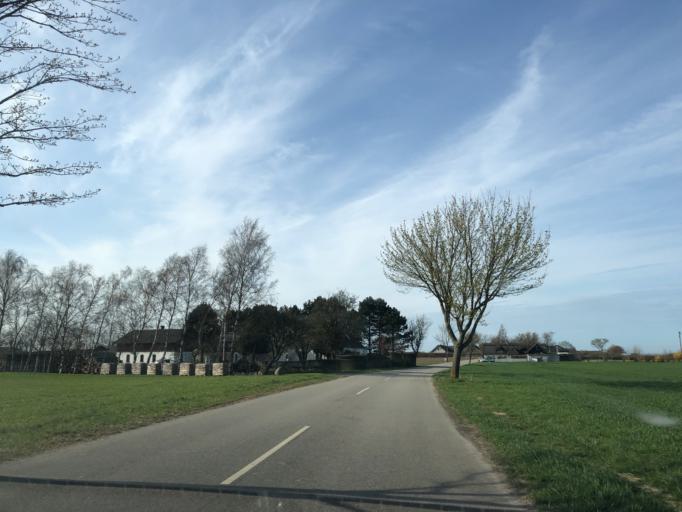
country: DK
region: Zealand
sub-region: Stevns Kommune
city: Store Heddinge
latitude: 55.2997
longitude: 12.4399
